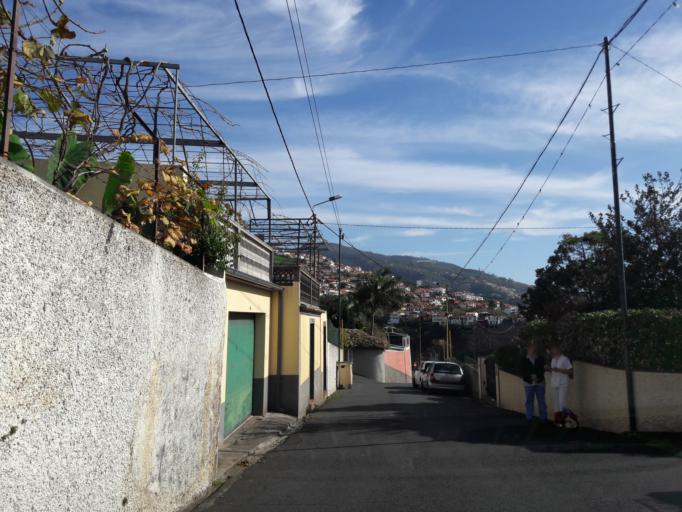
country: PT
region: Madeira
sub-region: Funchal
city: Nossa Senhora do Monte
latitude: 32.6685
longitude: -16.9222
